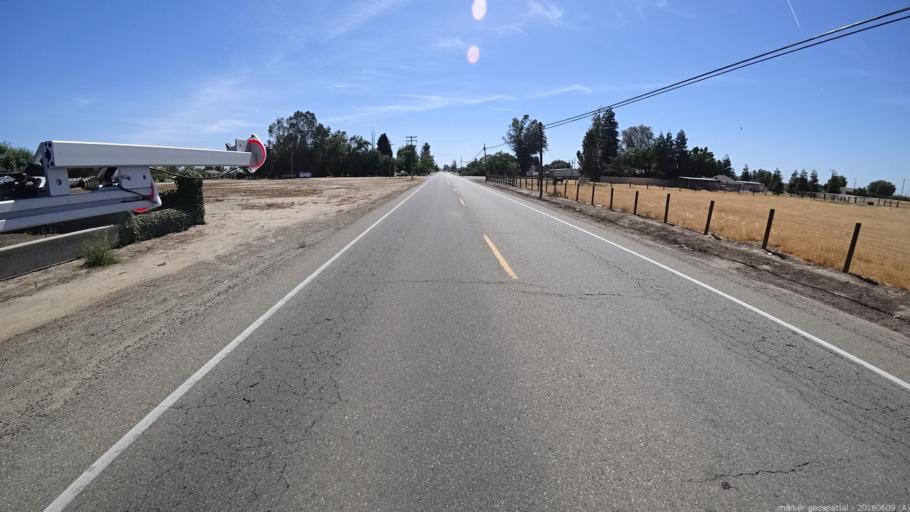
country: US
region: California
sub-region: Madera County
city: Madera
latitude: 36.9529
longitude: -120.1207
